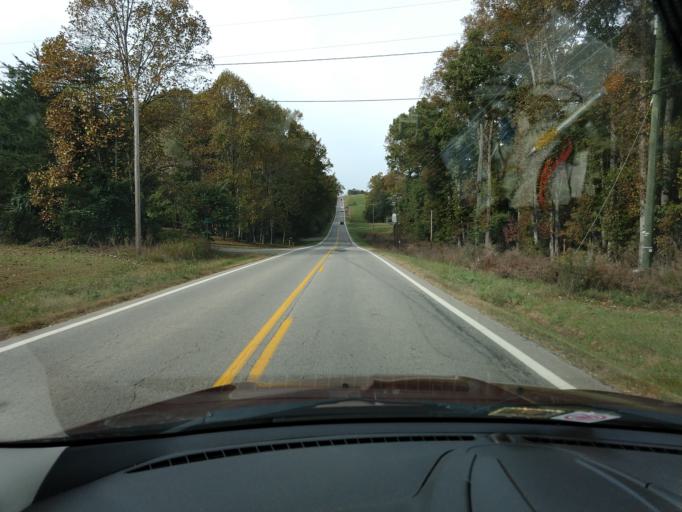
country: US
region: Virginia
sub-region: Pittsylvania County
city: Gretna
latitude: 36.9542
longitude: -79.4095
